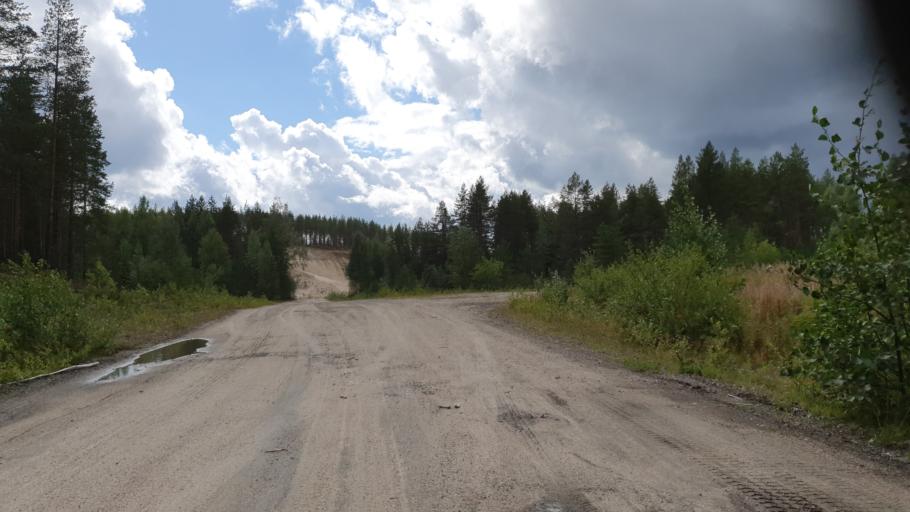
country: FI
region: Kainuu
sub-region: Kehys-Kainuu
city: Kuhmo
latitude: 64.1545
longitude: 29.3788
